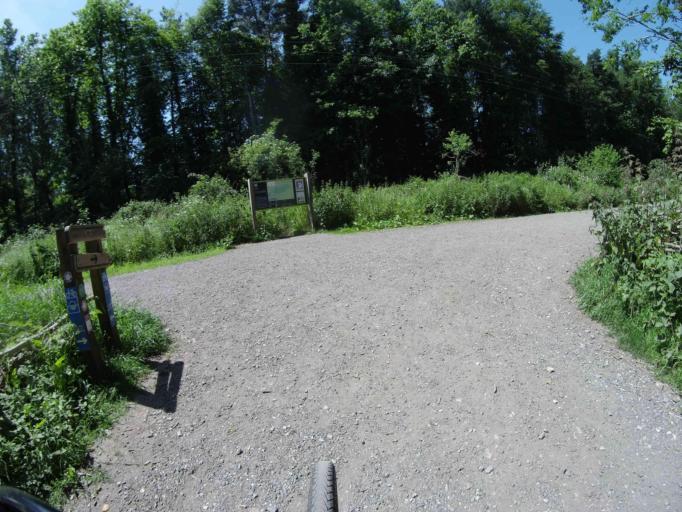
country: GB
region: England
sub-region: Devon
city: Bovey Tracey
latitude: 50.5945
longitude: -3.6816
